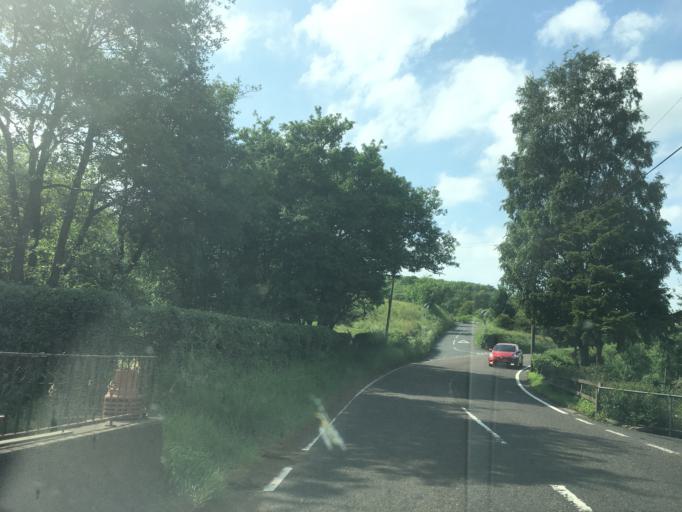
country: GB
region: Scotland
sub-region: South Lanarkshire
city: Dalserf
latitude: 55.7163
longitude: -3.8914
